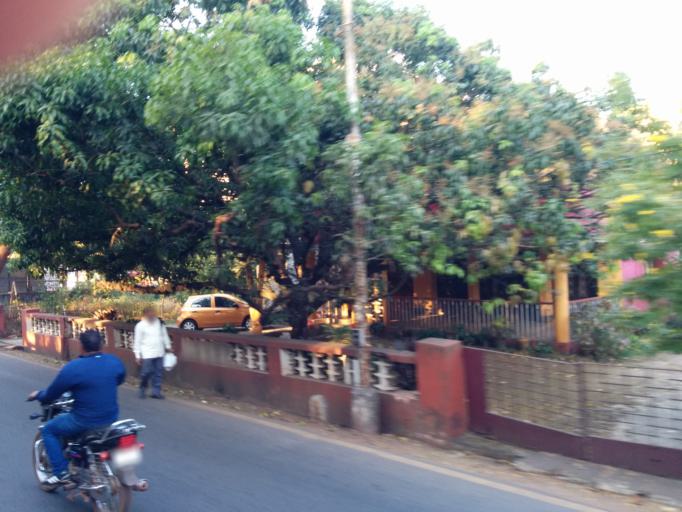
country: IN
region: Goa
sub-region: South Goa
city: Madgaon
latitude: 15.2783
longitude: 73.9593
